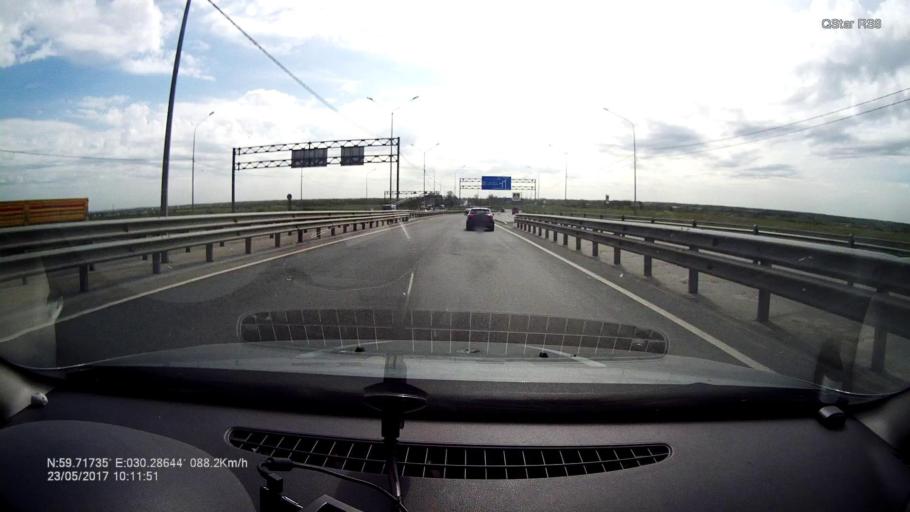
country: RU
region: St.-Petersburg
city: Aleksandrovskaya
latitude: 59.7172
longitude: 30.2873
